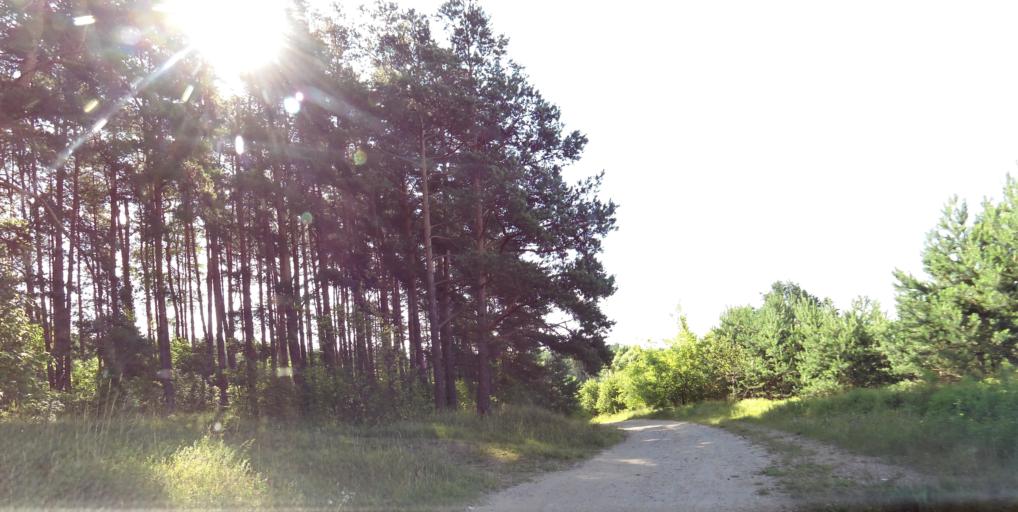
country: LT
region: Vilnius County
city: Pilaite
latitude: 54.6991
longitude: 25.1809
